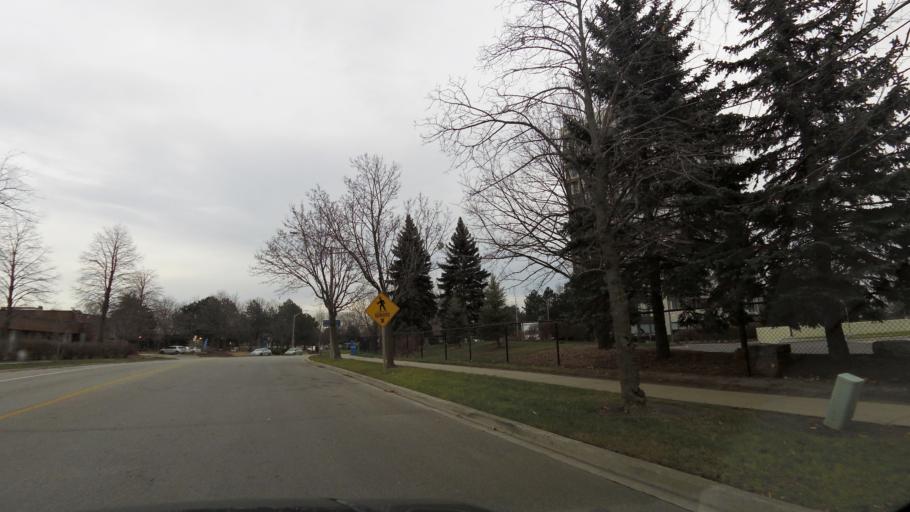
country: CA
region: Ontario
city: Etobicoke
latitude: 43.6256
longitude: -79.6017
